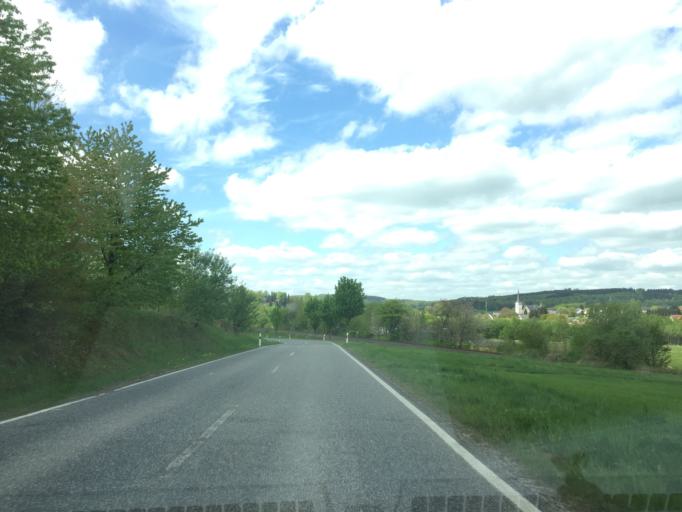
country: DE
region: Rheinland-Pfalz
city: Meudt
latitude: 50.4896
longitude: 7.9053
